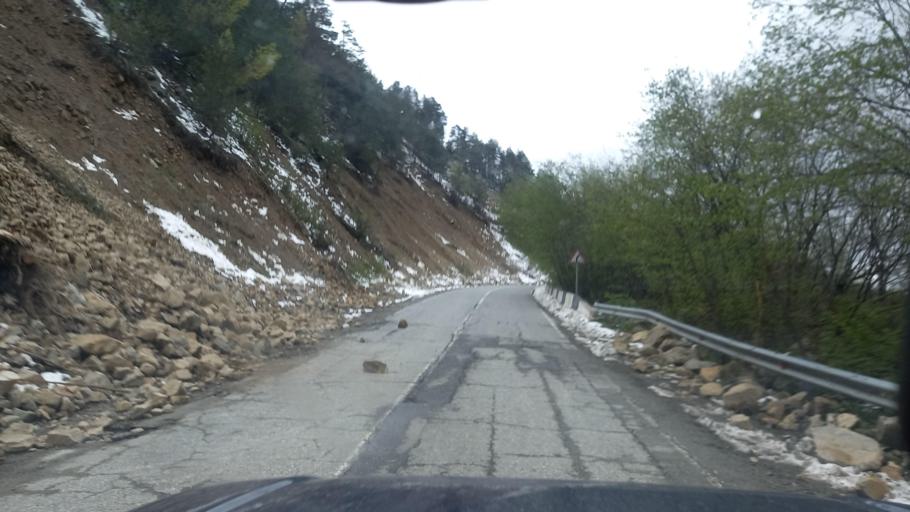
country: RU
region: North Ossetia
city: Mizur
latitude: 42.7987
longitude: 43.9272
